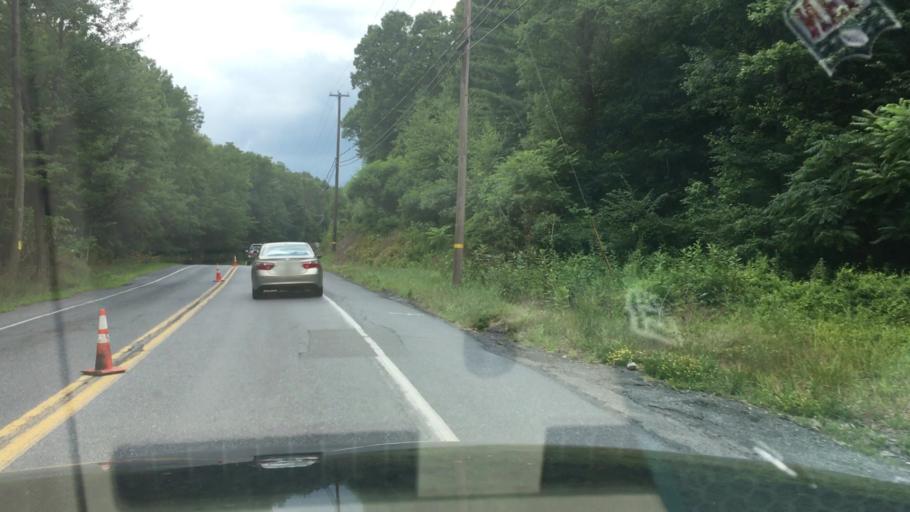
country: US
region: Pennsylvania
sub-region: Schuylkill County
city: Minersville
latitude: 40.6996
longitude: -76.2950
